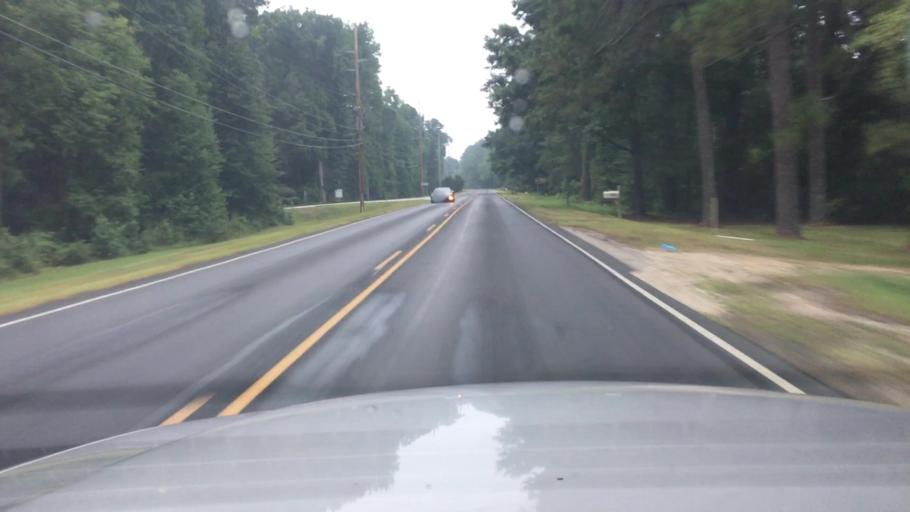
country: US
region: North Carolina
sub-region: Cumberland County
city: Fayetteville
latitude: 35.0043
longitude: -78.8609
